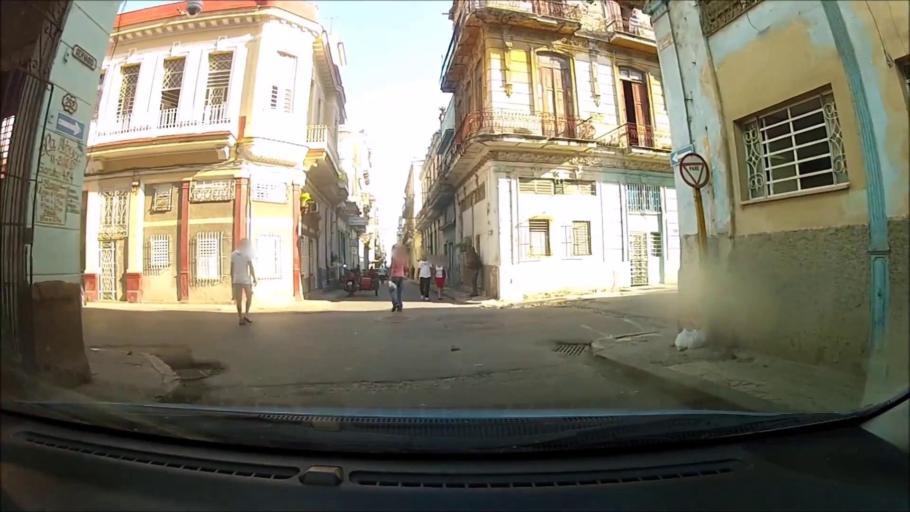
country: CU
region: La Habana
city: Centro Habana
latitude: 23.1381
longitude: -82.3691
